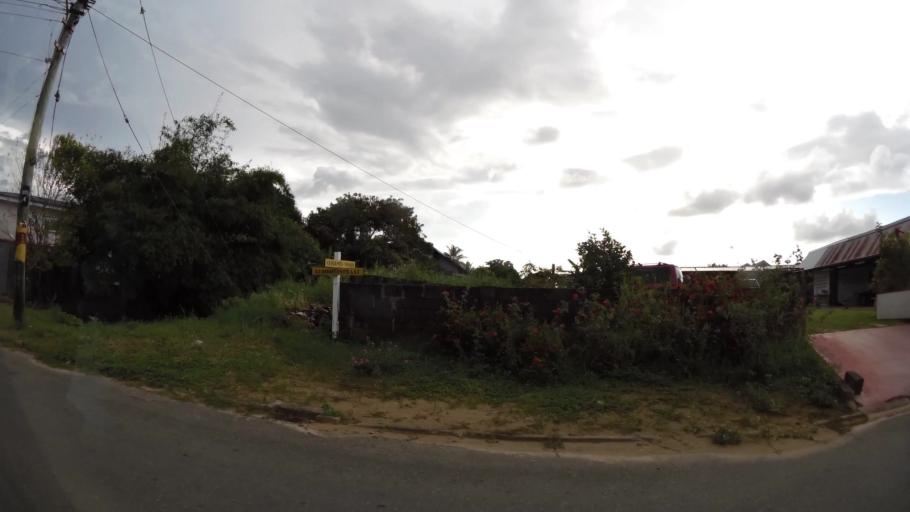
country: SR
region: Paramaribo
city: Paramaribo
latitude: 5.8392
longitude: -55.1774
